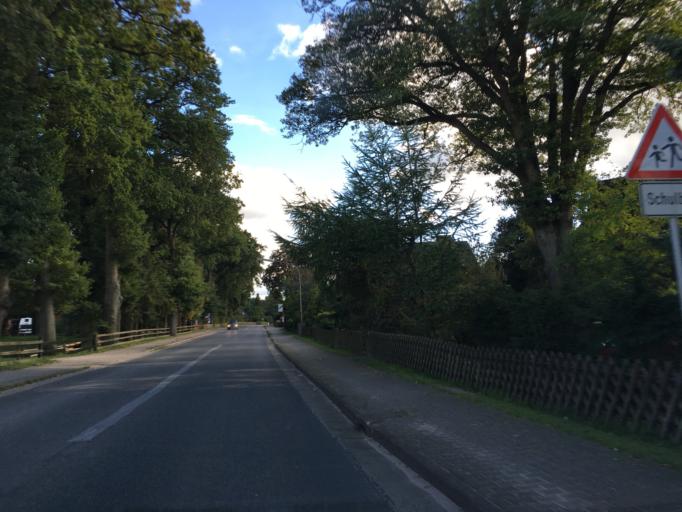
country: DE
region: Lower Saxony
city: Vierhofen
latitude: 53.2631
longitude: 10.2205
